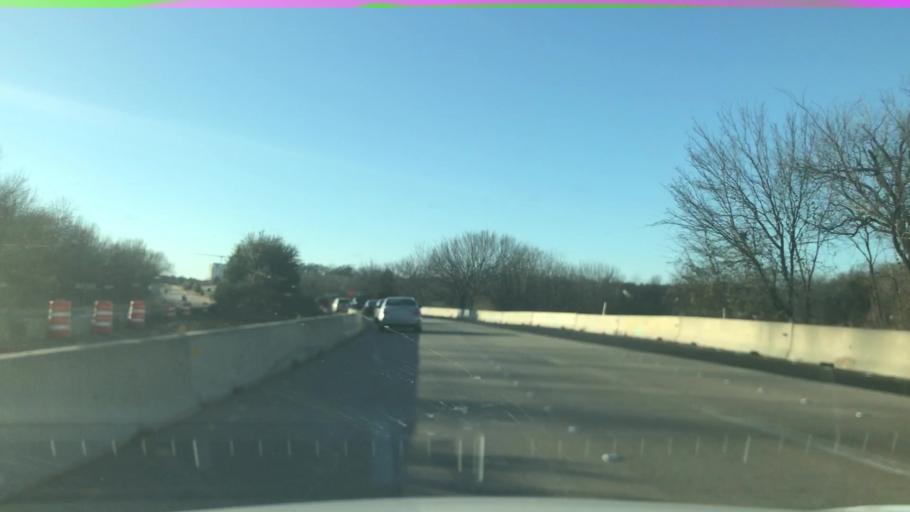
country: US
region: Texas
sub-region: Dallas County
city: Coppell
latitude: 32.9864
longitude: -97.0446
